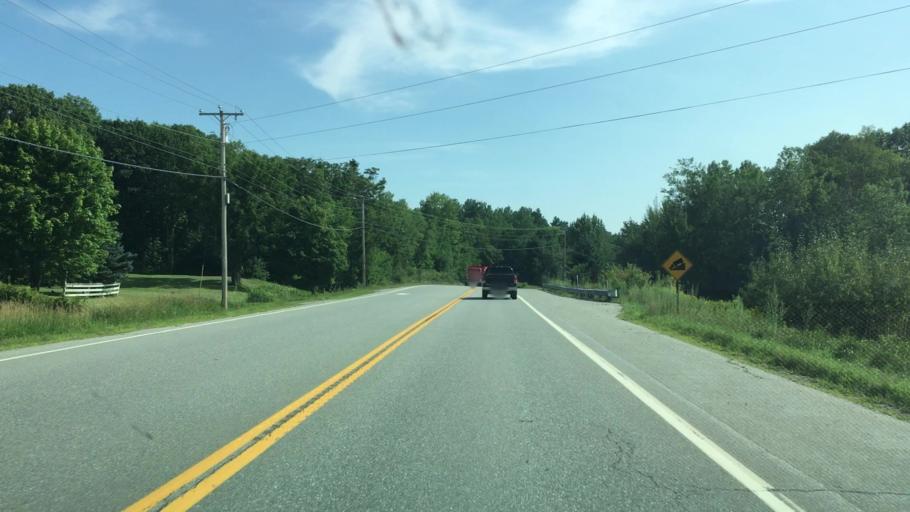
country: US
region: Maine
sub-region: Waldo County
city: Frankfort
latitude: 44.6148
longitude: -68.8696
